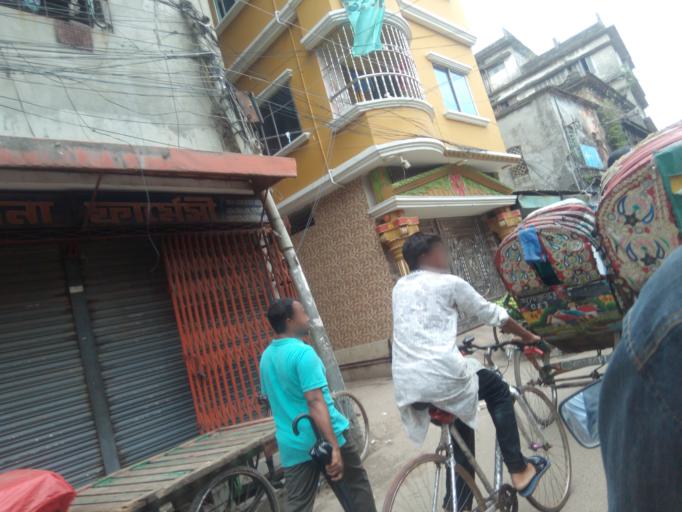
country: BD
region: Dhaka
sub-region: Dhaka
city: Dhaka
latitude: 23.7039
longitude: 90.4182
